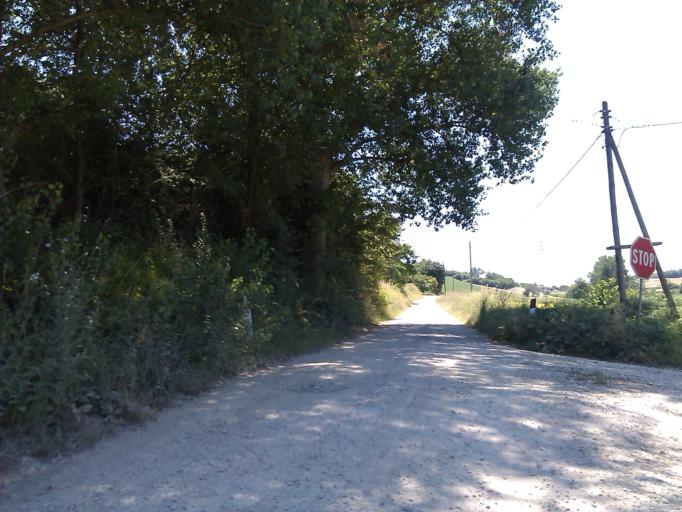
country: IT
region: Umbria
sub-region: Provincia di Terni
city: Ficulle
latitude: 42.8460
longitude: 12.0420
